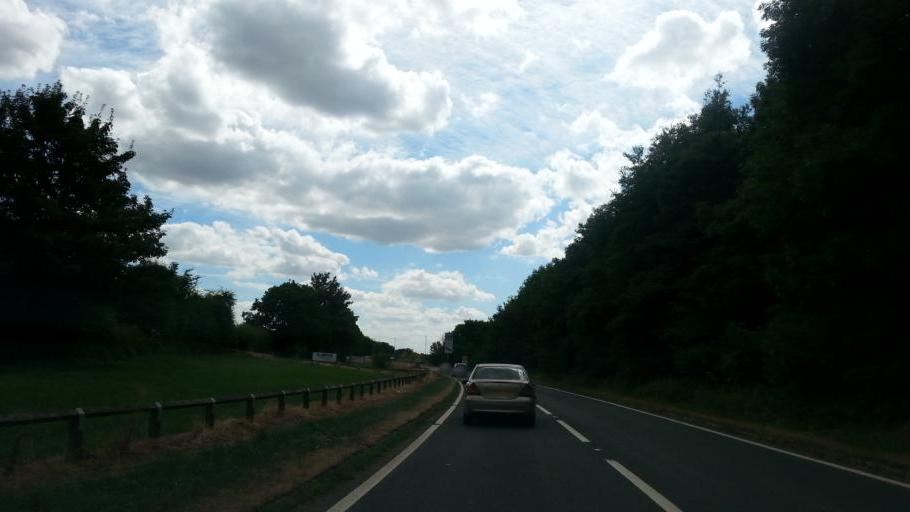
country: GB
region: England
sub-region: Northamptonshire
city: Silverstone
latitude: 52.0987
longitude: -1.0182
